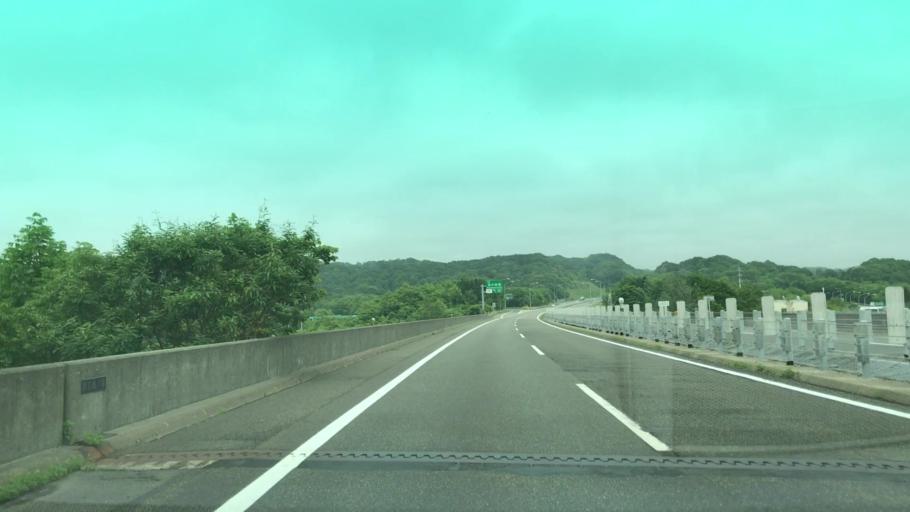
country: JP
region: Hokkaido
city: Tomakomai
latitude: 42.6294
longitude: 141.4854
